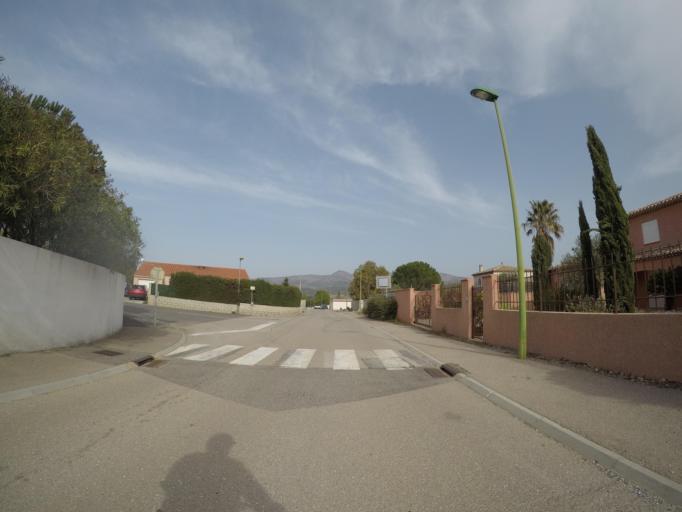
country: FR
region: Languedoc-Roussillon
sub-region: Departement des Pyrenees-Orientales
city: Baixas
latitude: 42.7745
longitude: 2.7949
